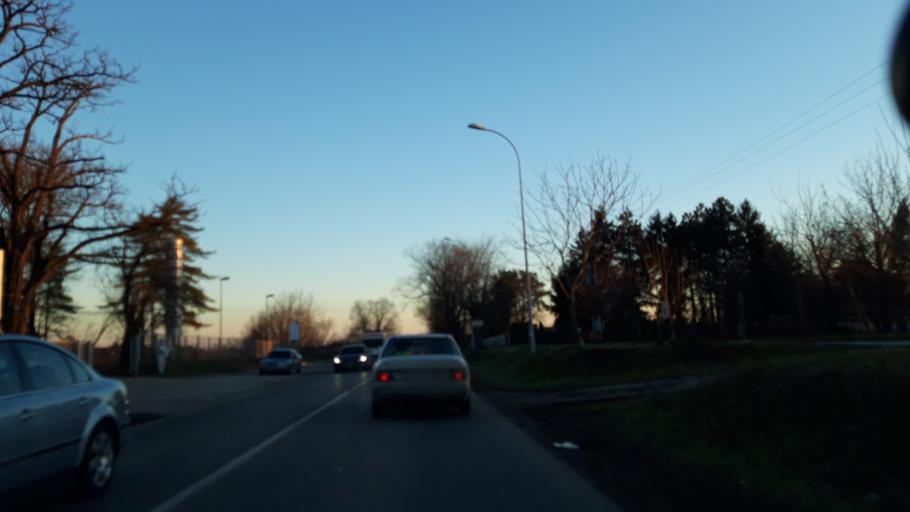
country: RS
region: Autonomna Pokrajina Vojvodina
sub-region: Sremski Okrug
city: Ingija
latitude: 45.0585
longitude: 20.0632
